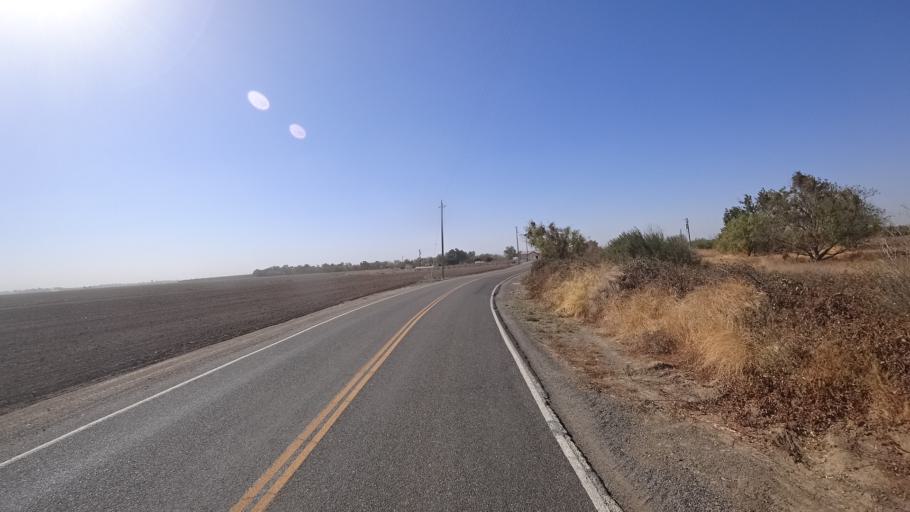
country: US
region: California
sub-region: Yolo County
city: Davis
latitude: 38.5901
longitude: -121.8107
